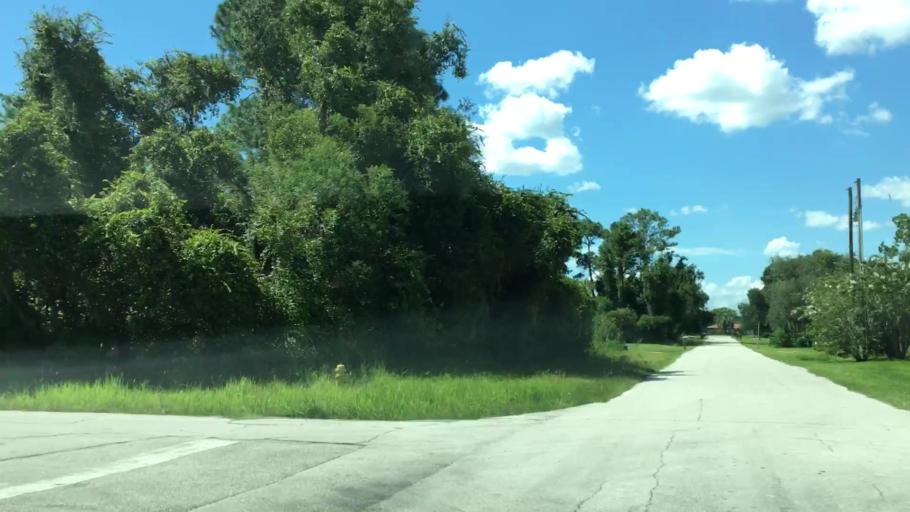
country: US
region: Florida
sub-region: Volusia County
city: Deltona
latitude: 28.8806
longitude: -81.2252
